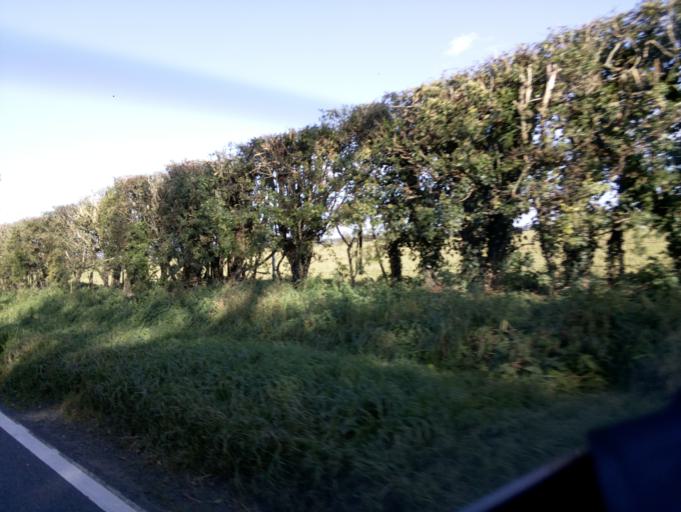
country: GB
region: England
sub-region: Hampshire
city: Swanmore
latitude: 50.9845
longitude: -1.1241
